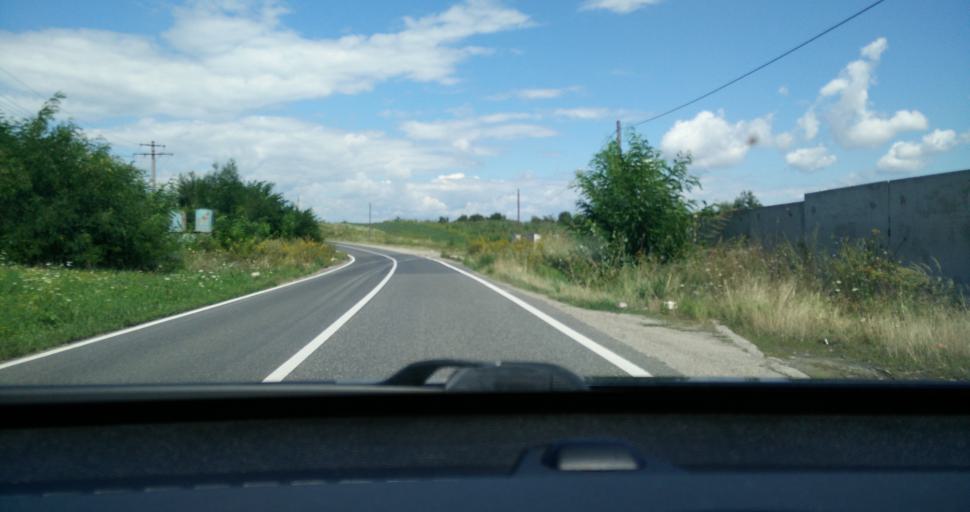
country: RO
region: Alba
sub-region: Comuna Sasciori
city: Sebesel
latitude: 45.8977
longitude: 23.5602
